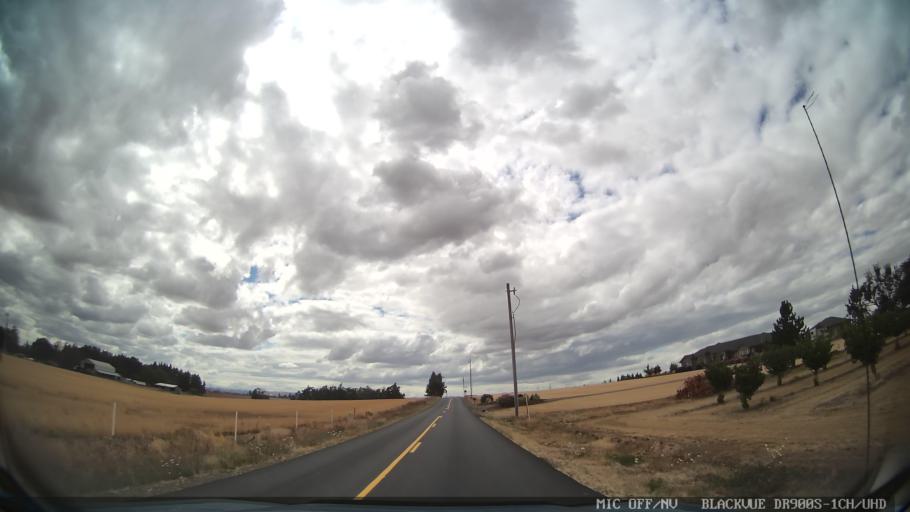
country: US
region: Oregon
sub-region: Marion County
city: Sublimity
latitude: 44.8404
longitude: -122.7903
